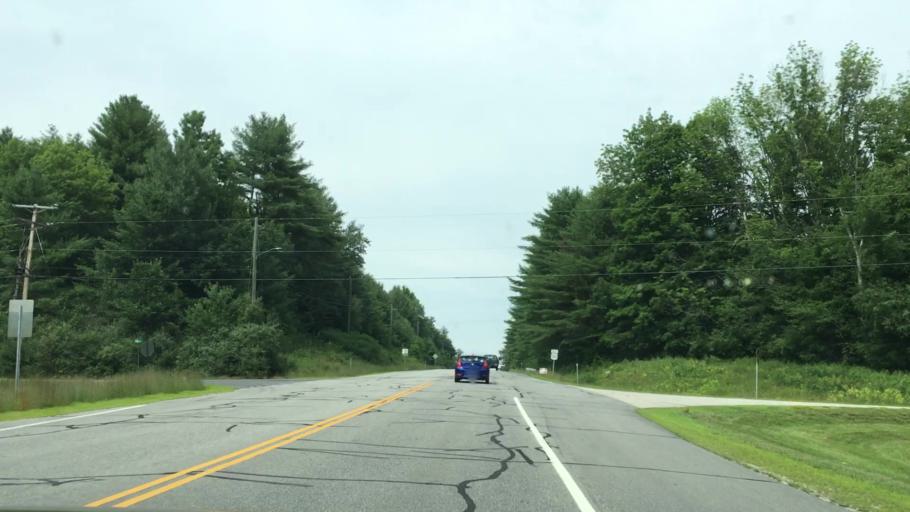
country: US
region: New Hampshire
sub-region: Hillsborough County
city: Antrim
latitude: 43.0520
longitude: -71.9249
